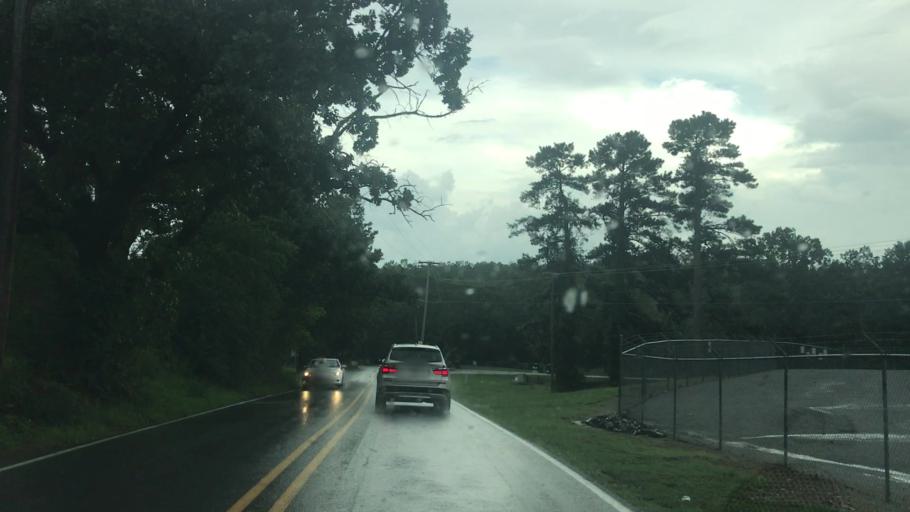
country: US
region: Arkansas
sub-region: Garland County
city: Rockwell
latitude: 34.4618
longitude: -93.1399
